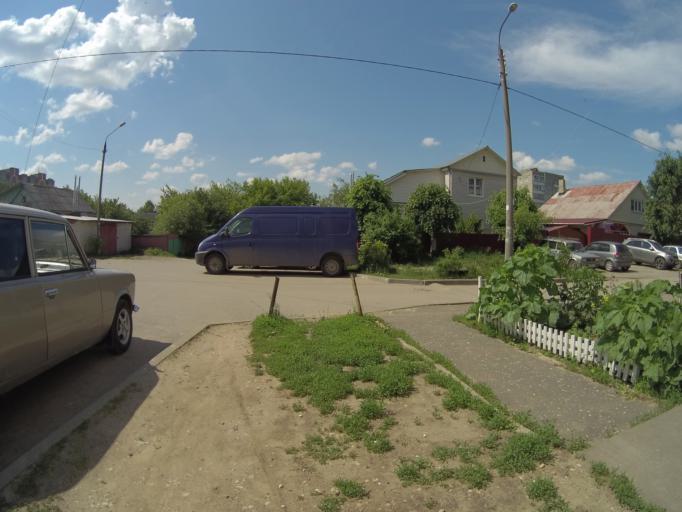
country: RU
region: Vladimir
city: Vladimir
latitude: 56.1281
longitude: 40.3501
